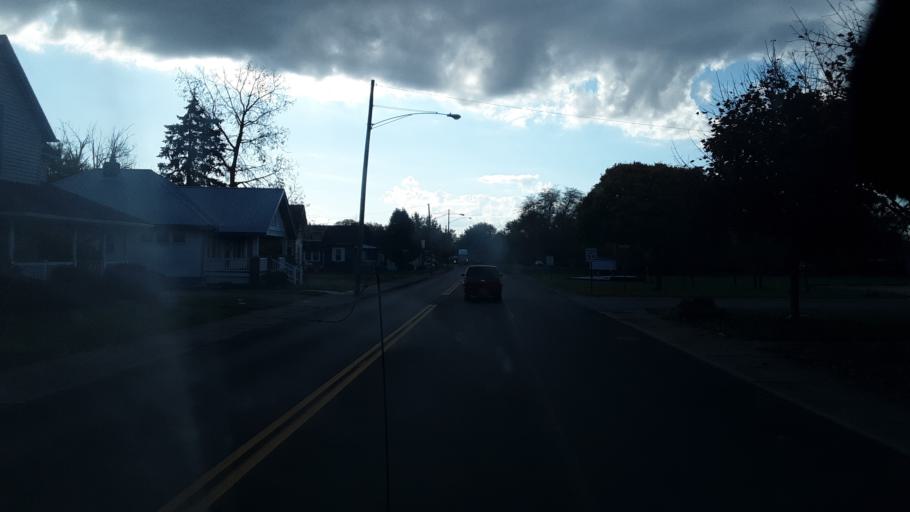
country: US
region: Ohio
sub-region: Fayette County
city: Washington Court House
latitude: 39.5455
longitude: -83.4465
